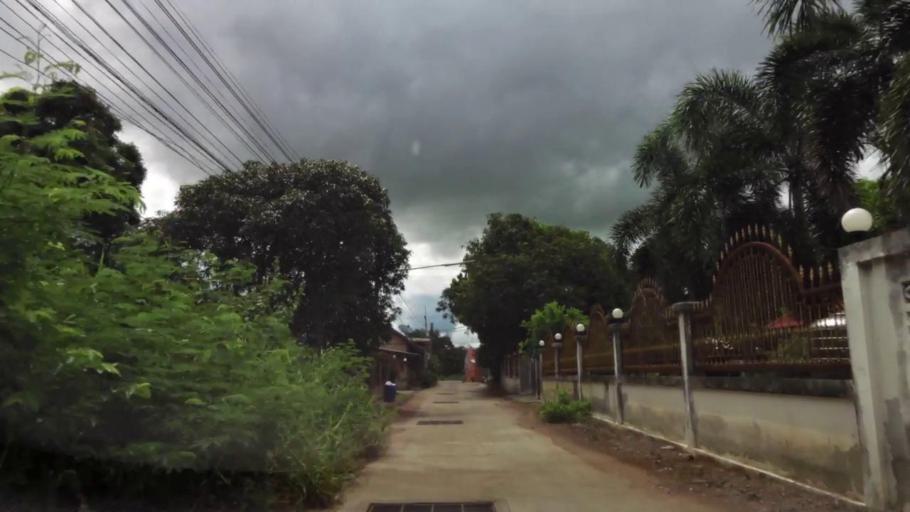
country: TH
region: Nakhon Sawan
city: Phai Sali
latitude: 15.6003
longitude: 100.6587
